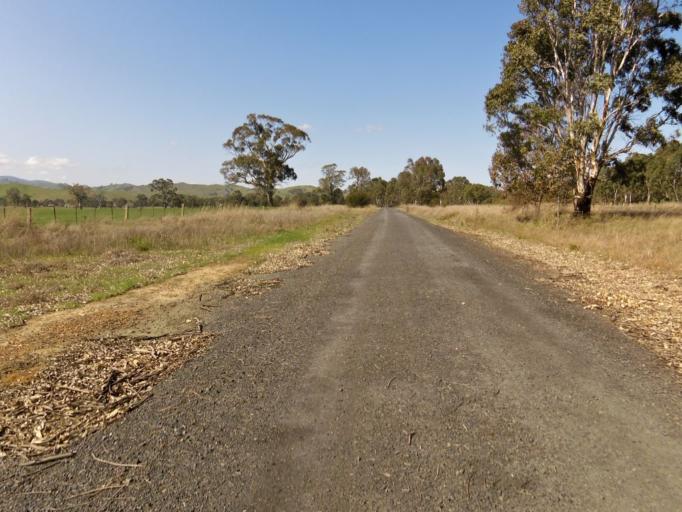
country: AU
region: Victoria
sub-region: Murrindindi
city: Alexandra
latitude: -37.0137
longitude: 145.7718
